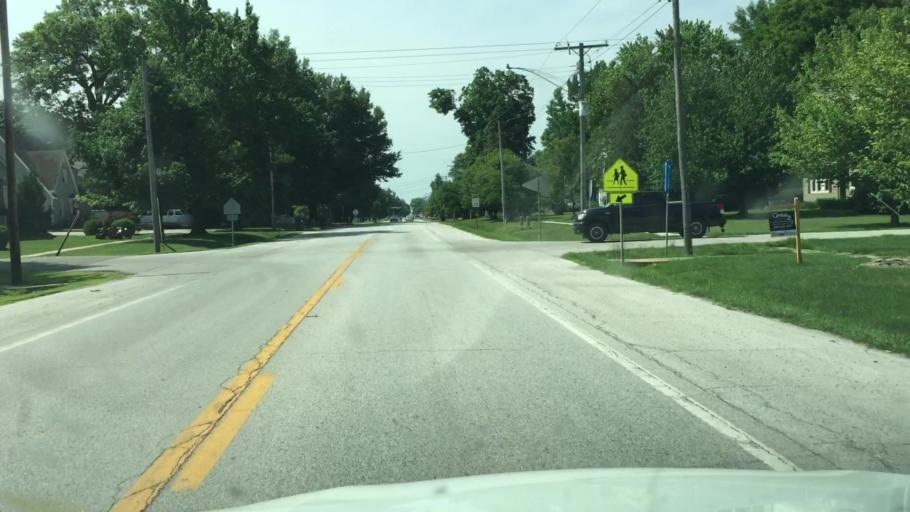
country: US
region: Illinois
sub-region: Hancock County
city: Carthage
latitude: 40.4208
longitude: -91.1362
